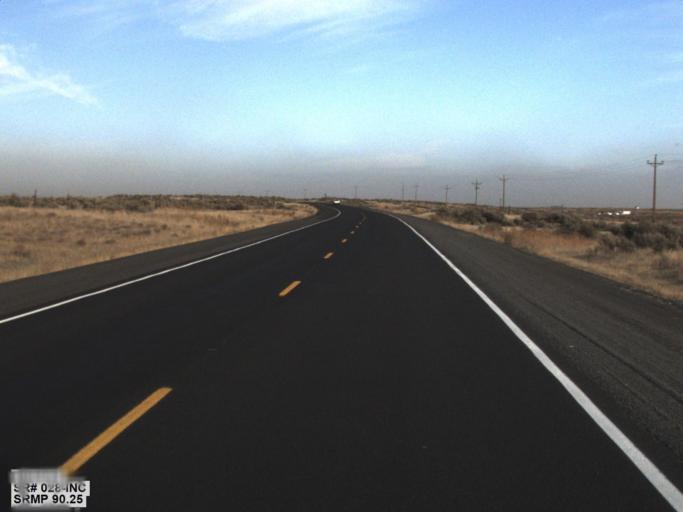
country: US
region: Washington
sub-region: Adams County
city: Ritzville
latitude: 47.3129
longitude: -118.7590
